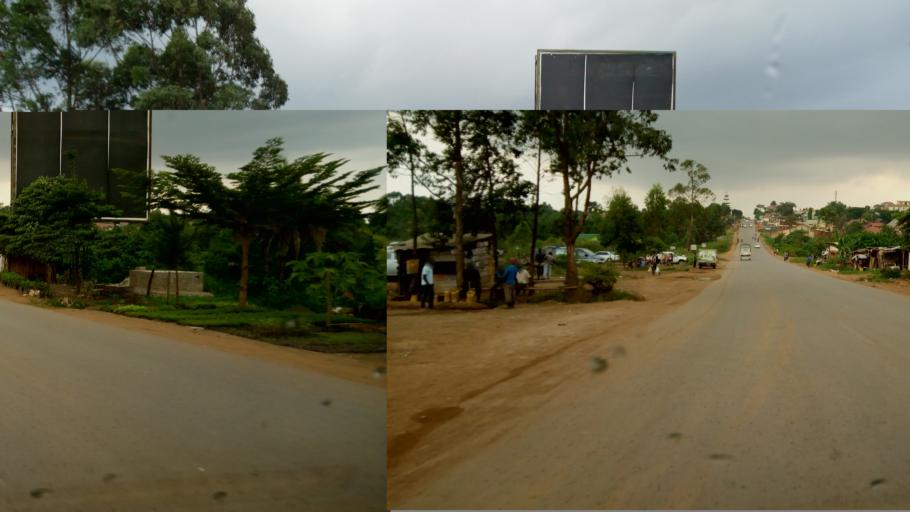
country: UG
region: Central Region
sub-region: Wakiso District
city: Wakiso
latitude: 0.4086
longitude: 32.5395
